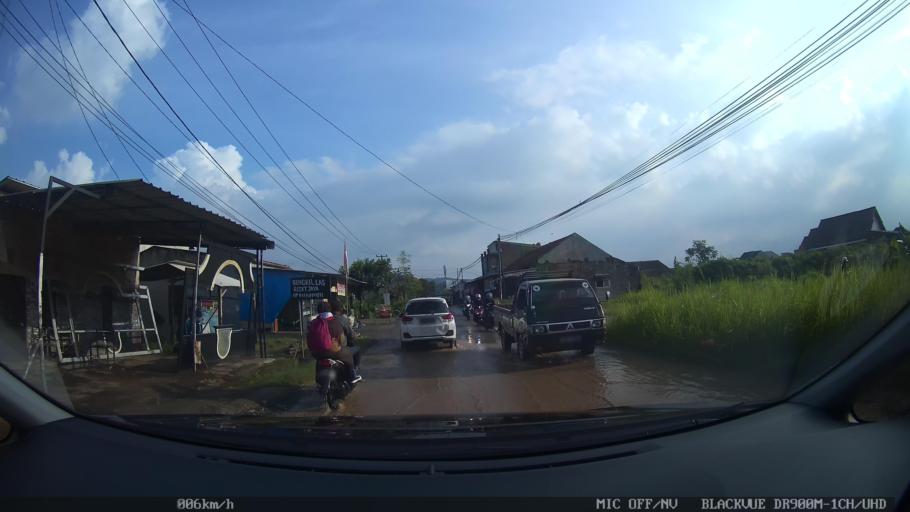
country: ID
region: Lampung
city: Kedaton
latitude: -5.3867
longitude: 105.3157
